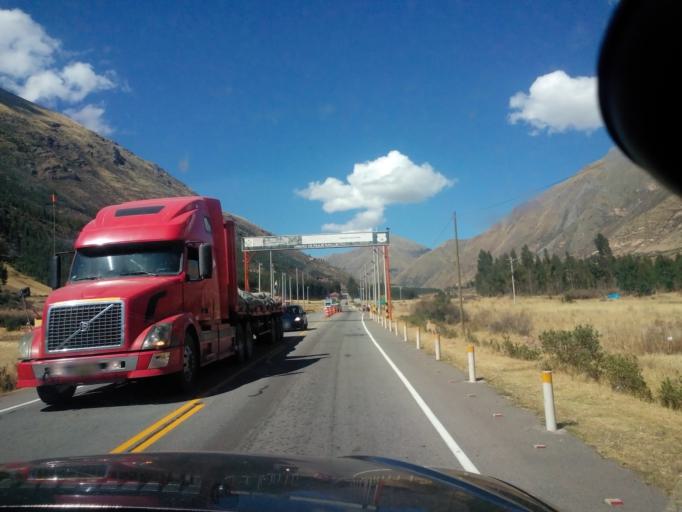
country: PE
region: Cusco
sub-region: Provincia de Quispicanchis
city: Cusipata
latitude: -13.9274
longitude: -71.5049
